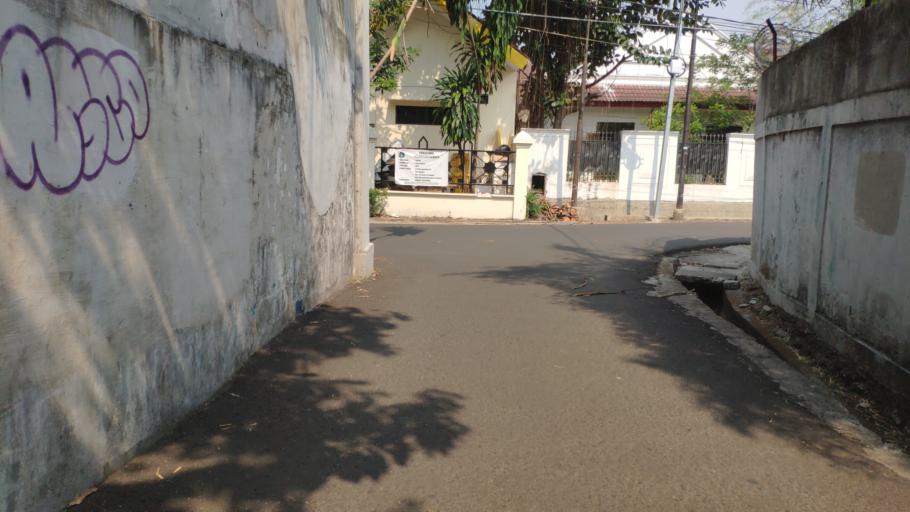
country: ID
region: Jakarta Raya
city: Jakarta
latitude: -6.2713
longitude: 106.8196
